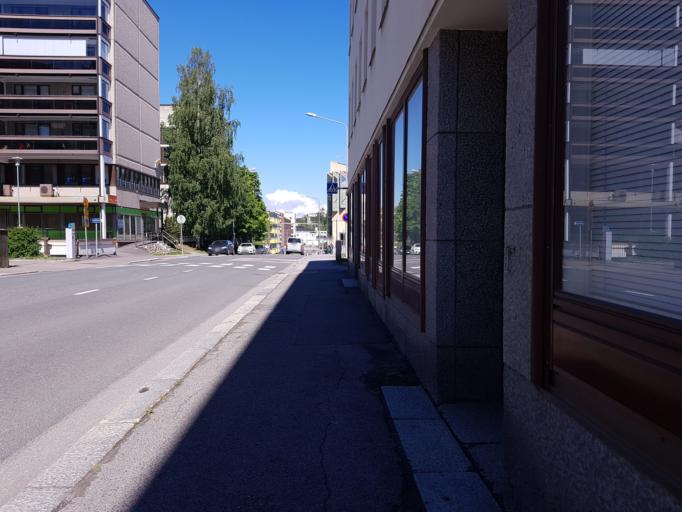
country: FI
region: Northern Savo
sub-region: Kuopio
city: Kuopio
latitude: 62.8940
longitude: 27.6820
